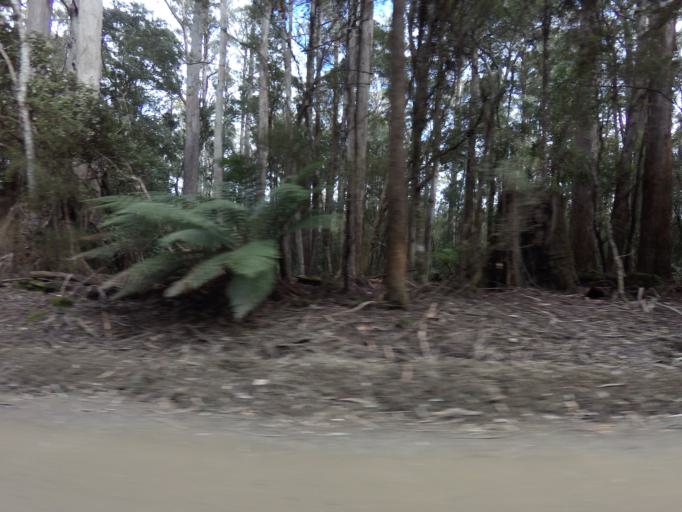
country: AU
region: Tasmania
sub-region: Huon Valley
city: Geeveston
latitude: -43.4000
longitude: 146.8612
